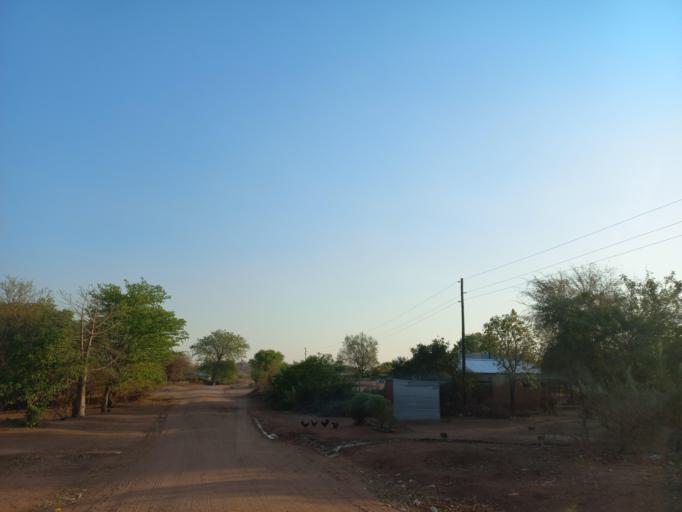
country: ZM
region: Lusaka
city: Luangwa
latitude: -15.6171
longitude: 30.3903
